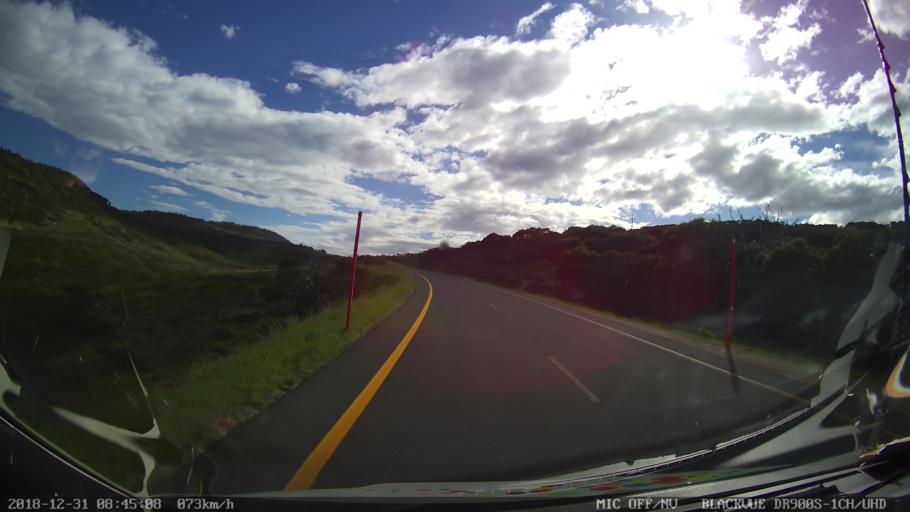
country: AU
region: New South Wales
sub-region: Snowy River
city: Jindabyne
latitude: -36.3785
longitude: 148.4619
